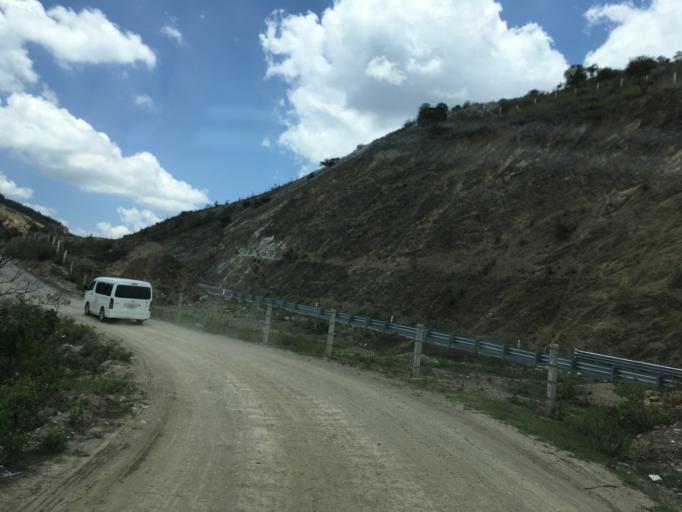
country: MX
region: Oaxaca
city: San Andres Sinaxtla
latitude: 17.5760
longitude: -97.3078
